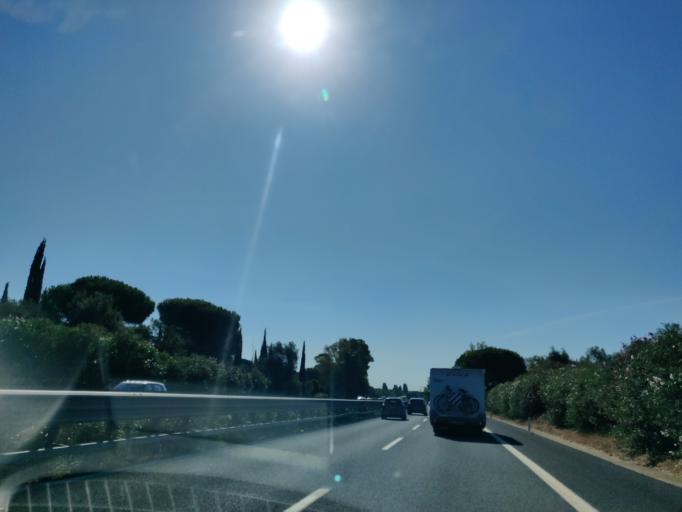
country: IT
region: Latium
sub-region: Citta metropolitana di Roma Capitale
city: Valcanneto
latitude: 41.9391
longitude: 12.1484
